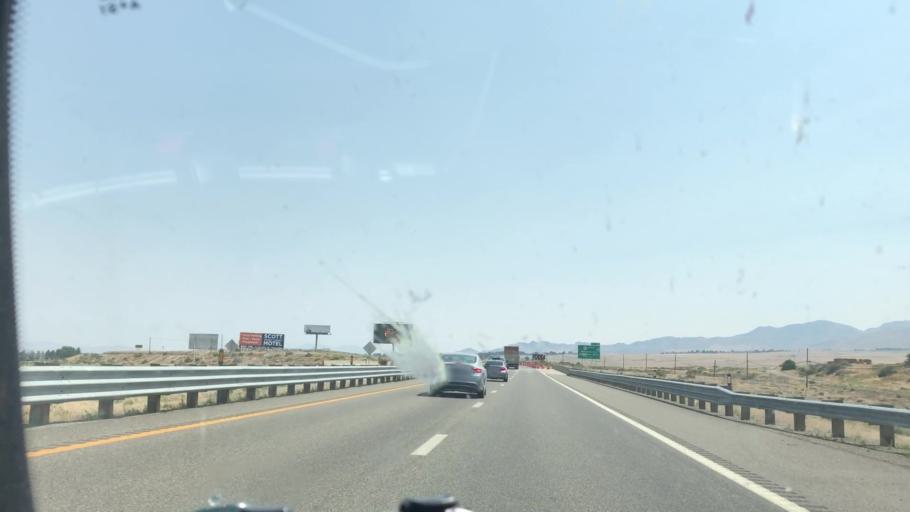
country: US
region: Nevada
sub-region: Humboldt County
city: Winnemucca
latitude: 40.9445
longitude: -117.7677
